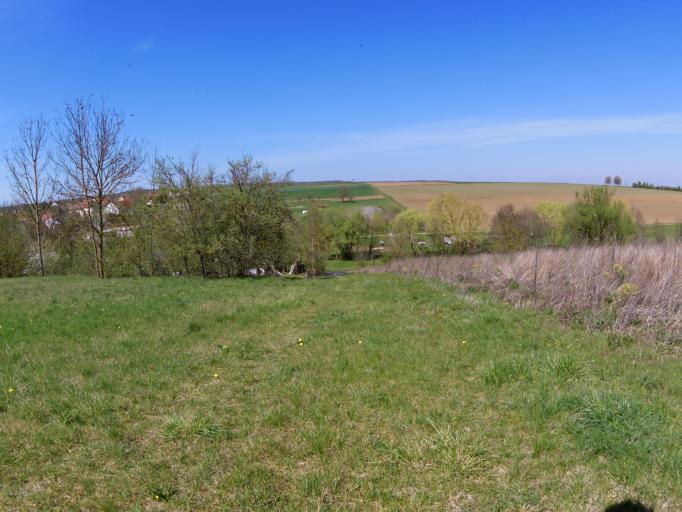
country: DE
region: Bavaria
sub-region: Regierungsbezirk Unterfranken
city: Kurnach
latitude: 49.8569
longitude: 10.0171
